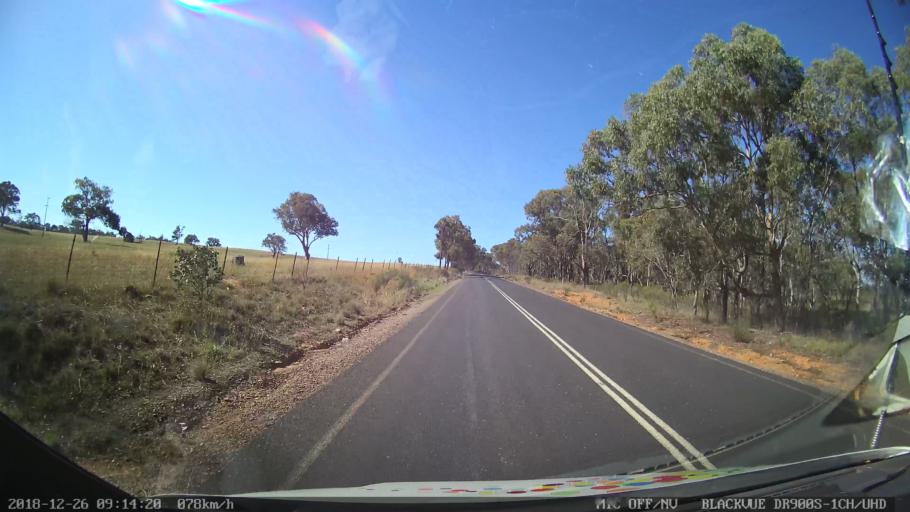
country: AU
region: New South Wales
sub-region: Mid-Western Regional
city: Kandos
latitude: -32.7775
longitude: 149.9788
